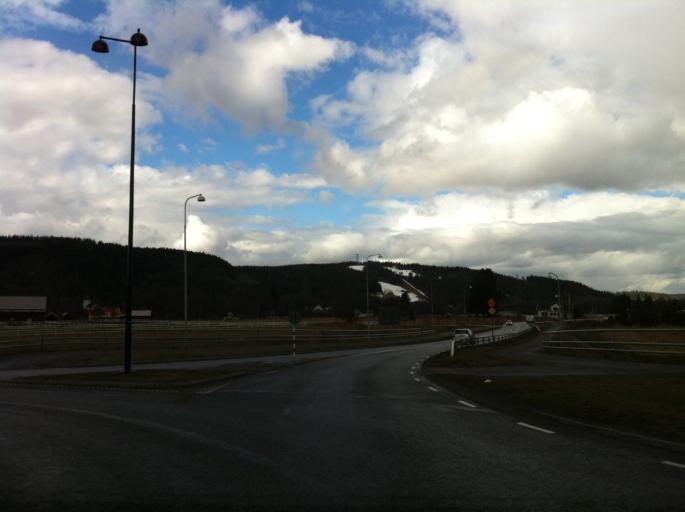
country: SE
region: Vaestra Goetaland
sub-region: Ulricehamns Kommun
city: Ulricehamn
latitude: 57.7440
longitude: 13.4272
